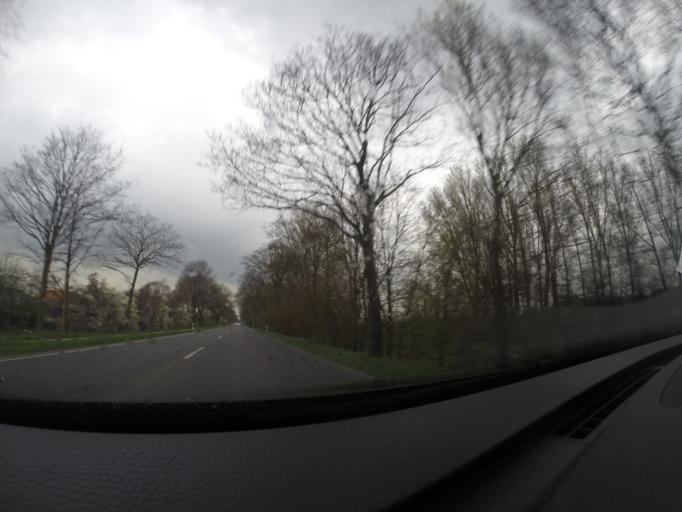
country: DE
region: North Rhine-Westphalia
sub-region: Regierungsbezirk Dusseldorf
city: Uedem
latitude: 51.7076
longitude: 6.3537
